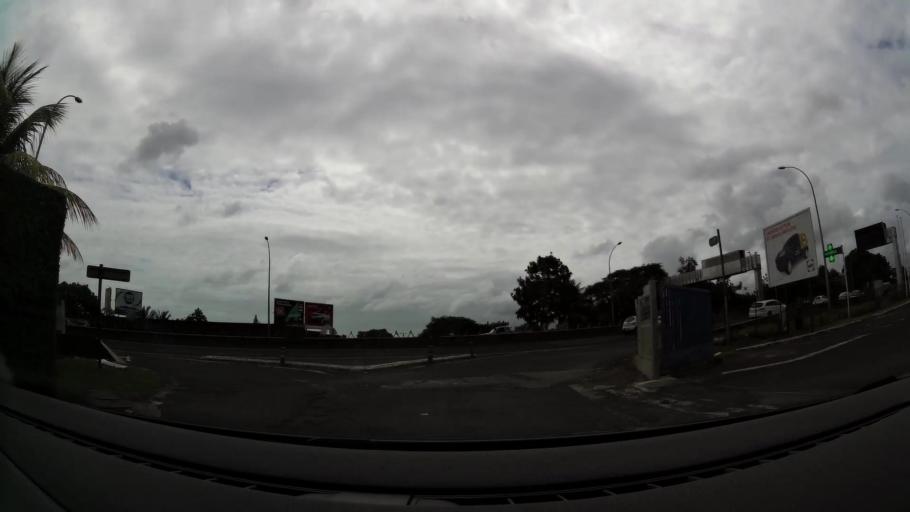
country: GP
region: Guadeloupe
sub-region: Guadeloupe
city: Baie-Mahault
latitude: 16.2531
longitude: -61.5802
